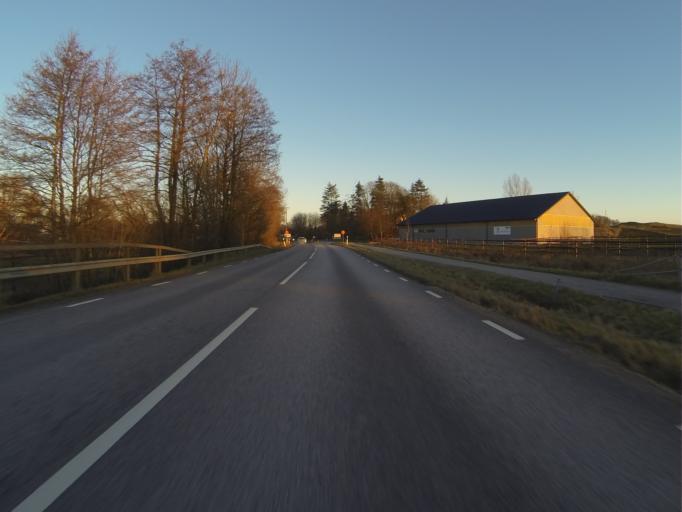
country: SE
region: Skane
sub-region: Eslovs Kommun
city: Eslov
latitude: 55.7535
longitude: 13.3523
